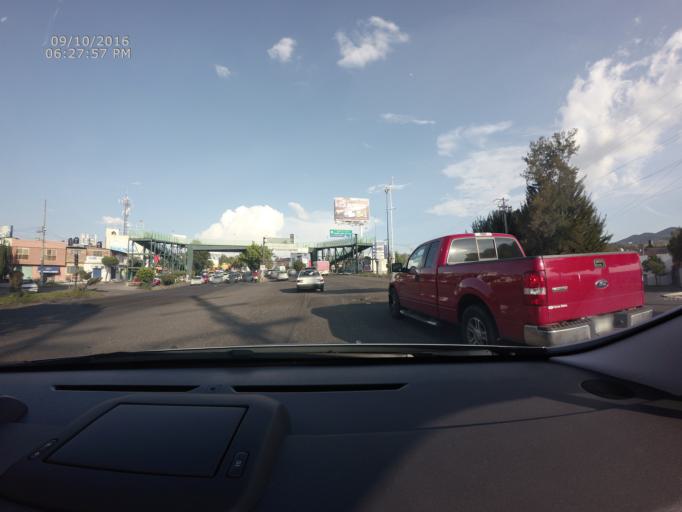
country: MX
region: Michoacan
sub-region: Morelia
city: Morelos
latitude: 19.6722
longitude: -101.2102
